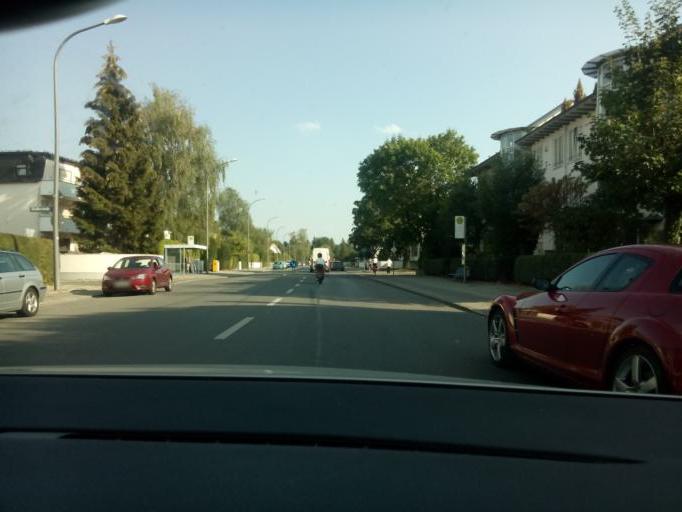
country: DE
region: Bavaria
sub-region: Upper Bavaria
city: Unterhaching
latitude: 48.0978
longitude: 11.6077
